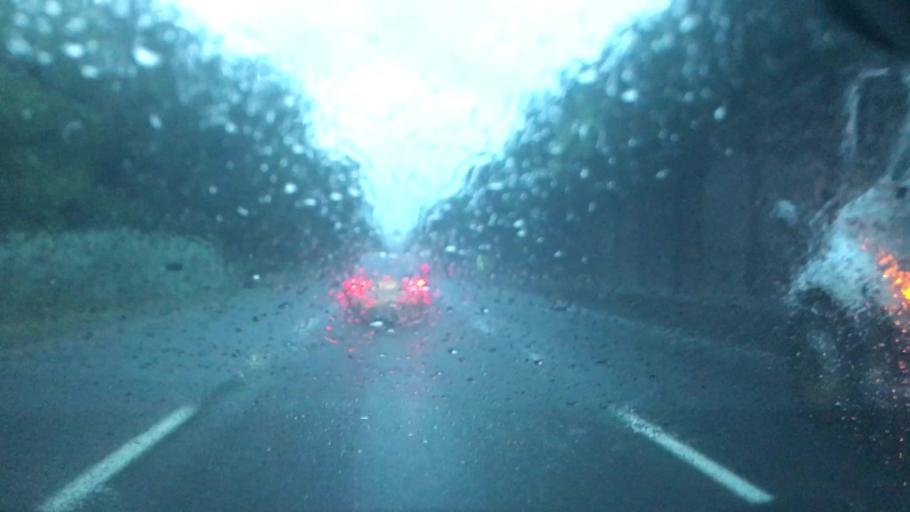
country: US
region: New Jersey
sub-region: Somerset County
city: Bernardsville
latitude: 40.7025
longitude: -74.5627
